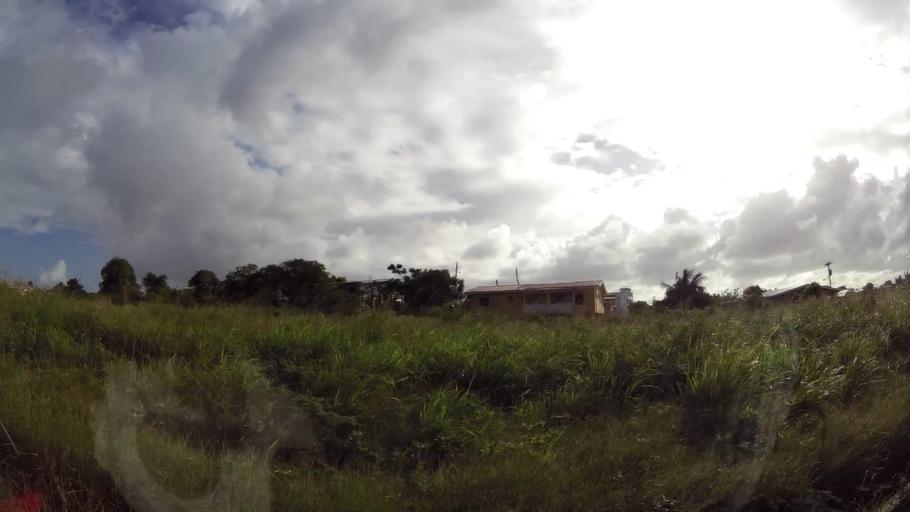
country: AG
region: Saint John
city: Saint John's
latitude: 17.1292
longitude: -61.8309
